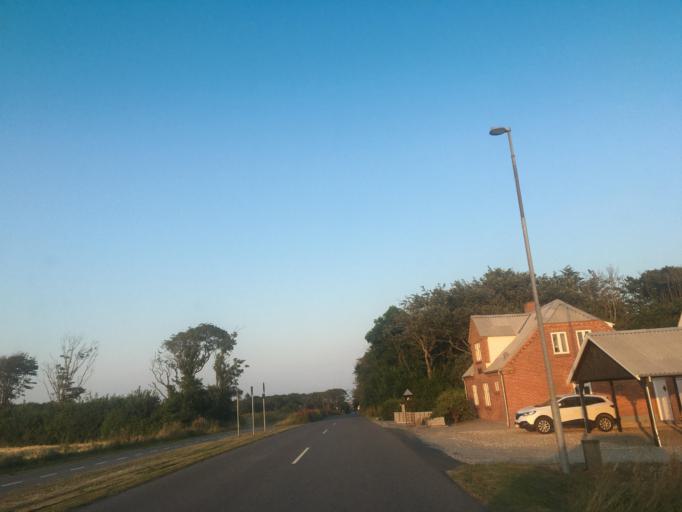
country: DK
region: North Denmark
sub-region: Thisted Kommune
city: Hurup
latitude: 56.7522
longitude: 8.3928
